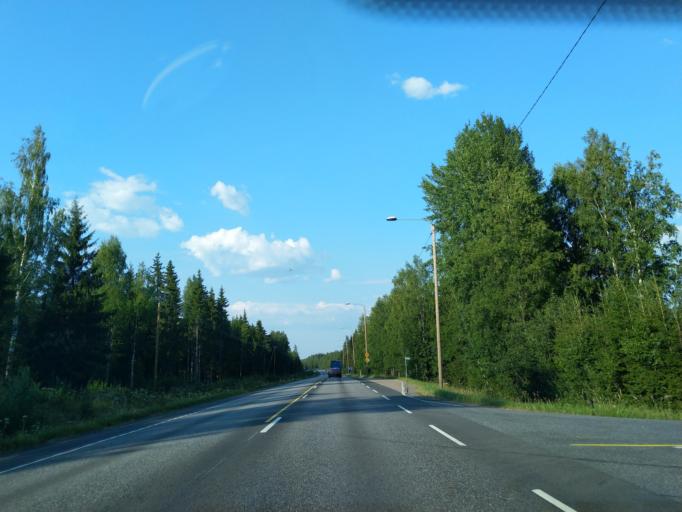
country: FI
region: Satakunta
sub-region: Pori
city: Pomarkku
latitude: 61.7073
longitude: 22.0274
